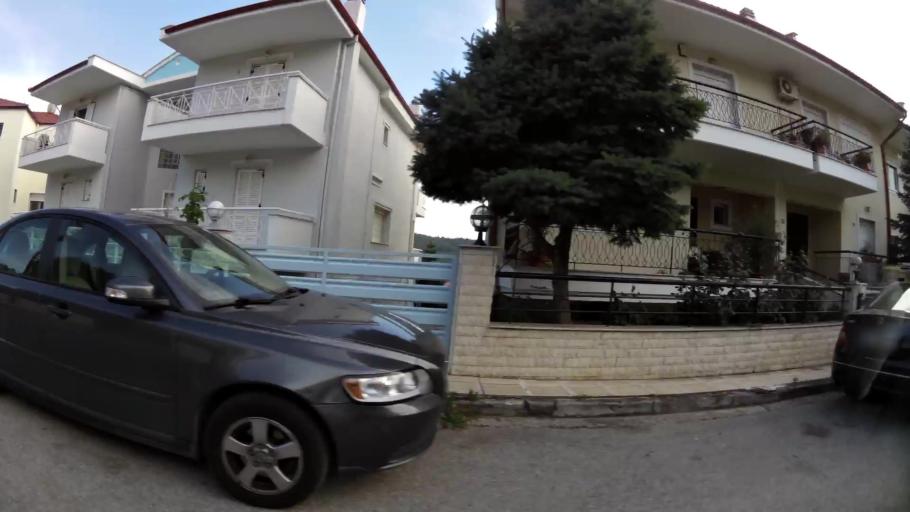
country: GR
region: Central Macedonia
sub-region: Nomos Thessalonikis
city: Pefka
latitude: 40.6572
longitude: 23.0012
